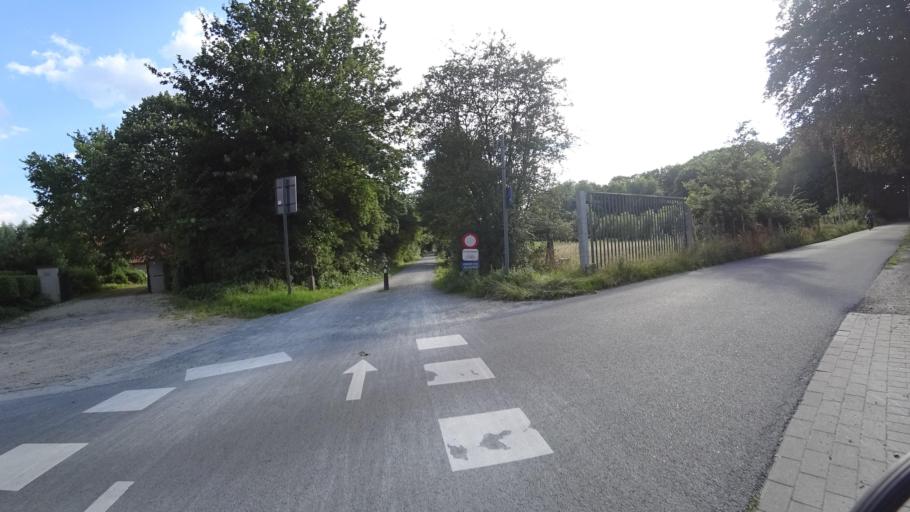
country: BE
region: Flanders
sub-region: Provincie West-Vlaanderen
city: Sint-Kruis
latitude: 51.1902
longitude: 3.2607
